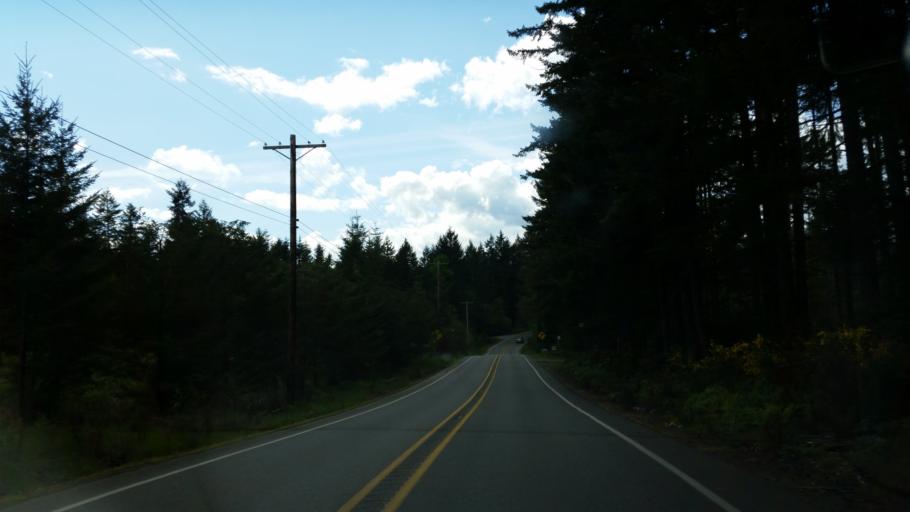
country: US
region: Washington
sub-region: Pierce County
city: Key Center
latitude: 47.3683
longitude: -122.7664
